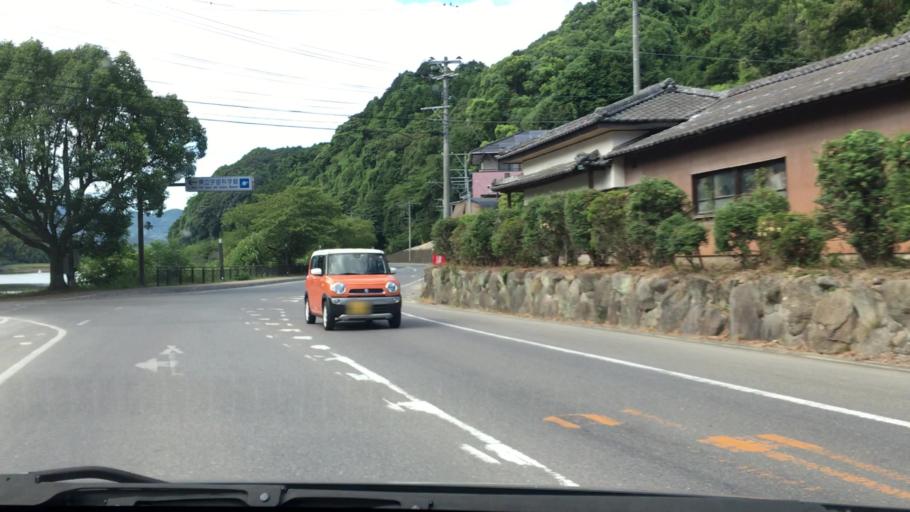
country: JP
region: Saga Prefecture
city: Takeocho-takeo
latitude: 33.1775
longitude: 130.0376
